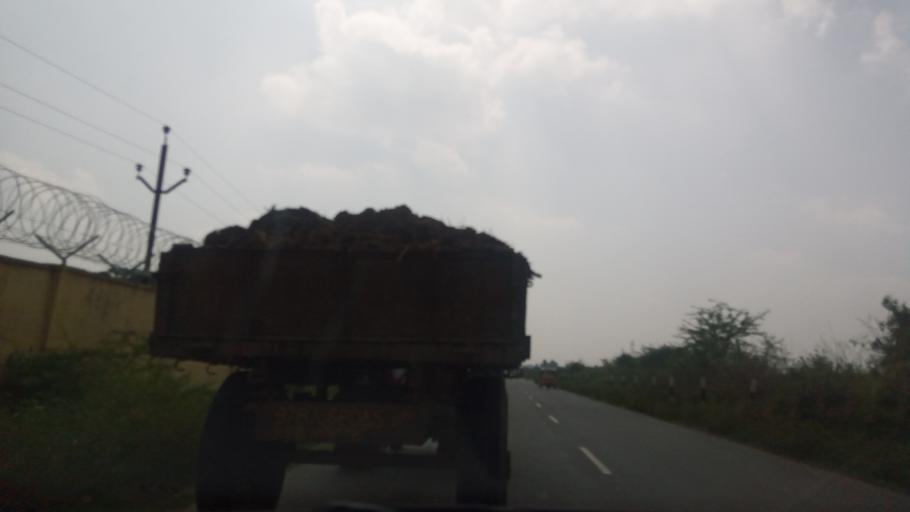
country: IN
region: Tamil Nadu
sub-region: Vellore
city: Arakkonam
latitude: 13.0514
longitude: 79.6743
